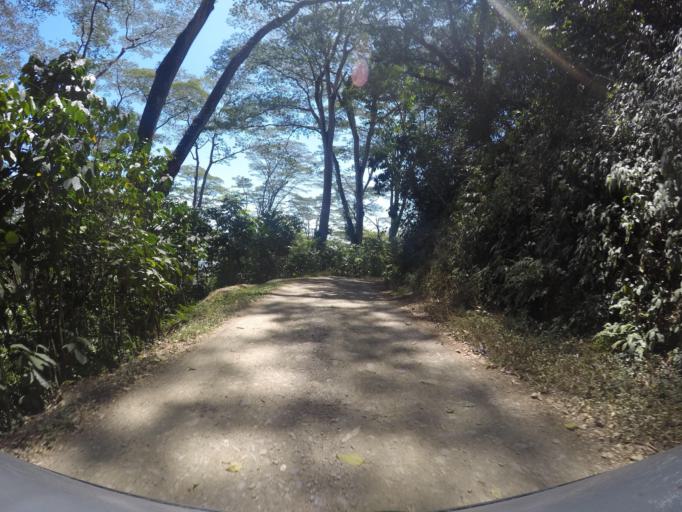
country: TL
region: Ermera
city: Gleno
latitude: -8.7378
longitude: 125.4085
